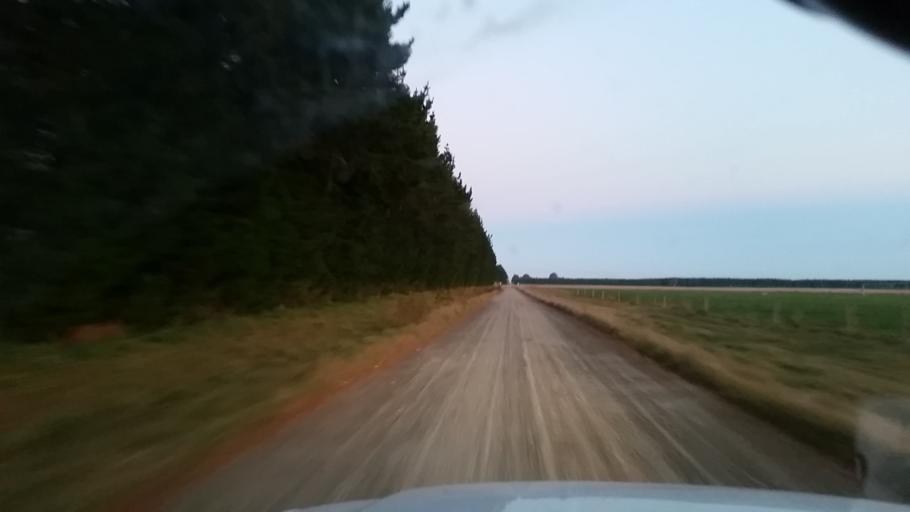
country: NZ
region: Canterbury
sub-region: Ashburton District
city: Tinwald
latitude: -43.9555
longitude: 171.6210
